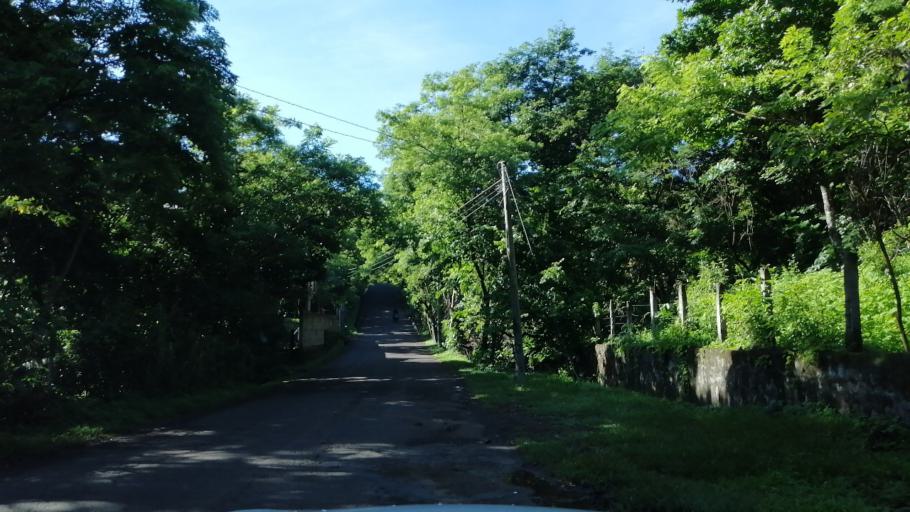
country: SV
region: Morazan
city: Cacaopera
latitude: 13.7683
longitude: -88.0691
